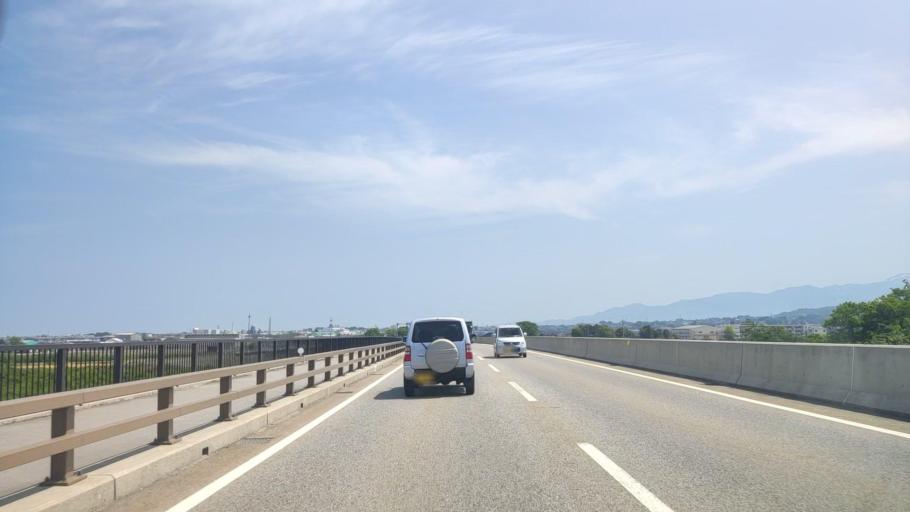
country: JP
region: Toyama
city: Uozu
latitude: 36.8522
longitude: 137.4252
